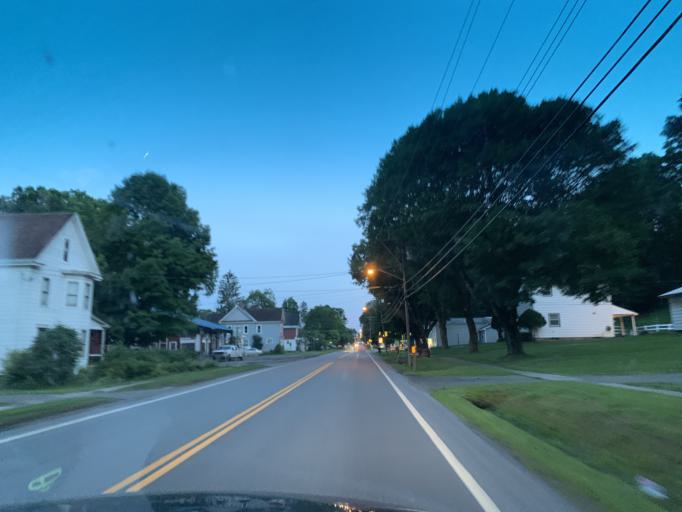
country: US
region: New York
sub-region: Chenango County
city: New Berlin
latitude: 42.6301
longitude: -75.3324
